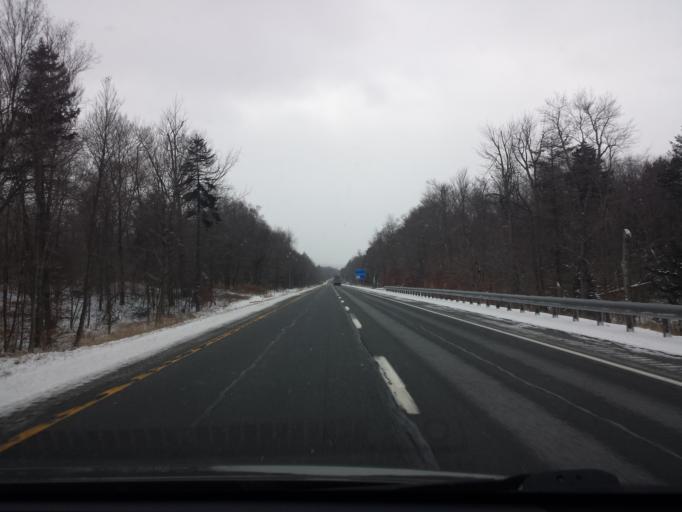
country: US
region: Pennsylvania
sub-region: Carbon County
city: Towamensing Trails
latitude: 41.0769
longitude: -75.5456
